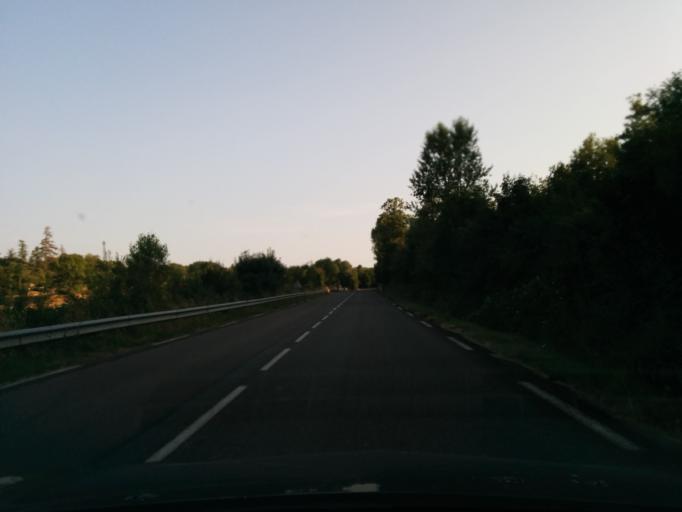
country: FR
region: Midi-Pyrenees
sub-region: Departement du Lot
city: Le Vigan
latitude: 44.6582
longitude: 1.4776
